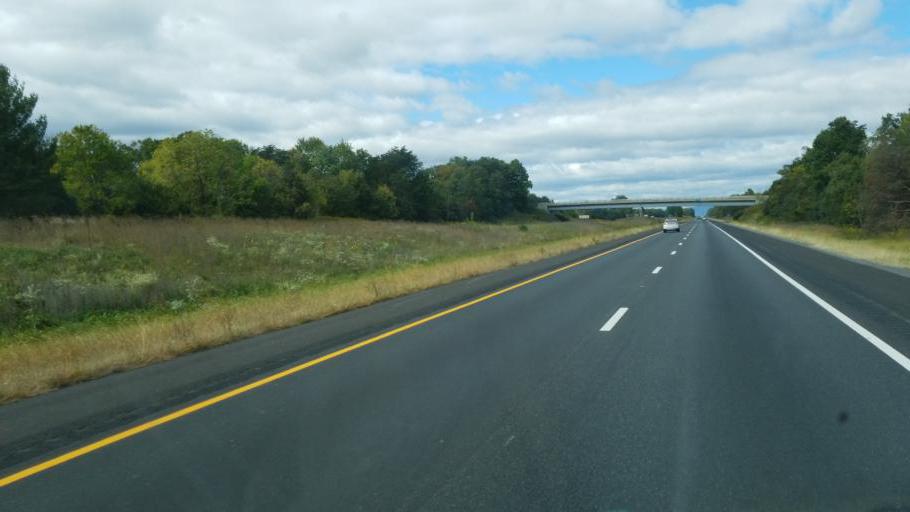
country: US
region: Virginia
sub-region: Warren County
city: Front Royal
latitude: 38.9720
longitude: -78.2102
